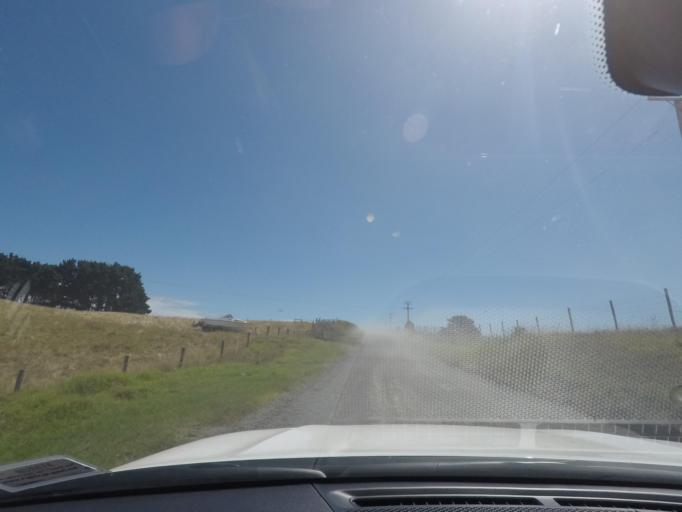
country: NZ
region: Auckland
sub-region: Auckland
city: Parakai
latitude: -36.5843
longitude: 174.2951
